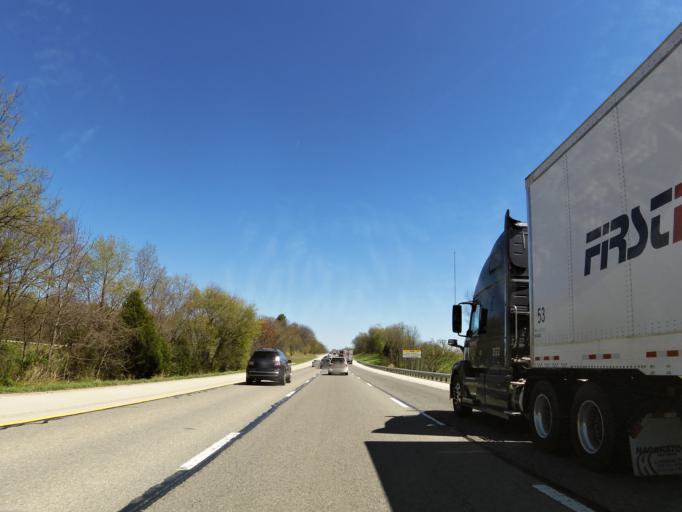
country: US
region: Kentucky
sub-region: Edmonson County
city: Brownsville
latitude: 37.0178
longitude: -86.2685
